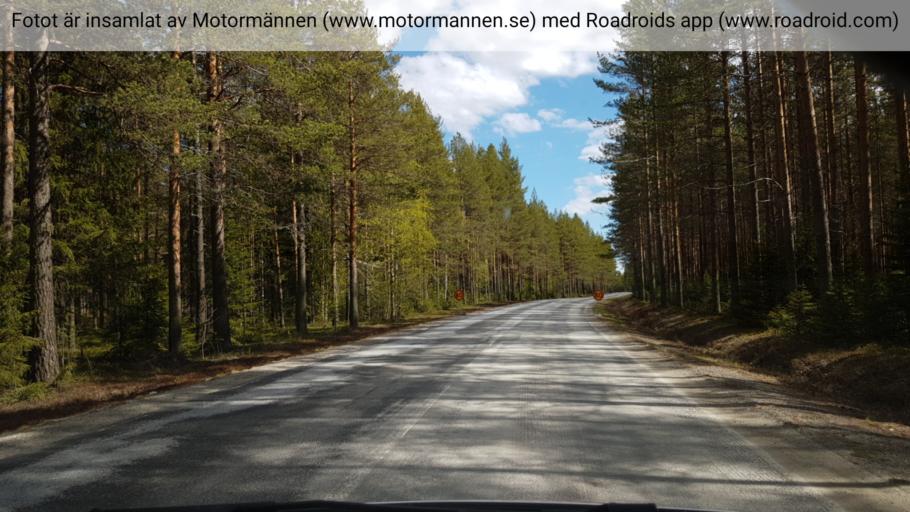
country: SE
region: Vaesterbotten
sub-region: Vindelns Kommun
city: Vindeln
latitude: 64.1726
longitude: 19.7479
